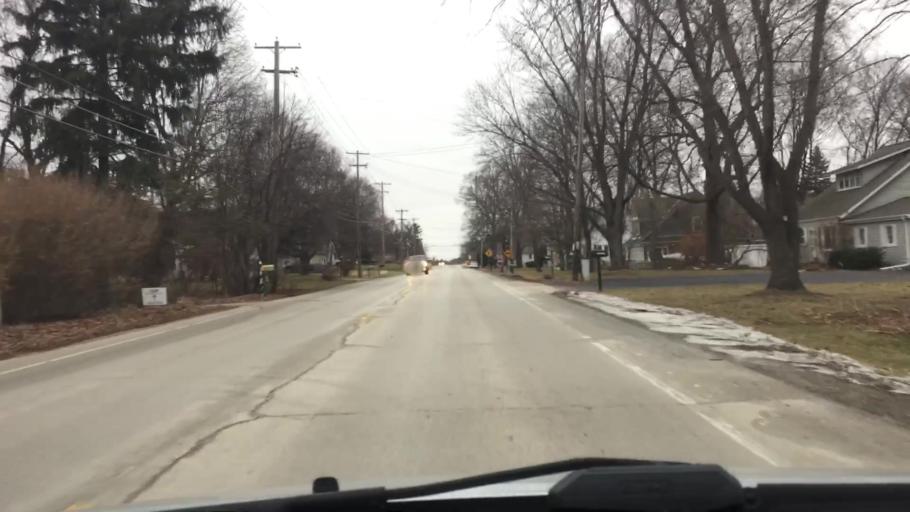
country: US
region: Wisconsin
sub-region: Waukesha County
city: Nashotah
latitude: 43.0956
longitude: -88.4030
